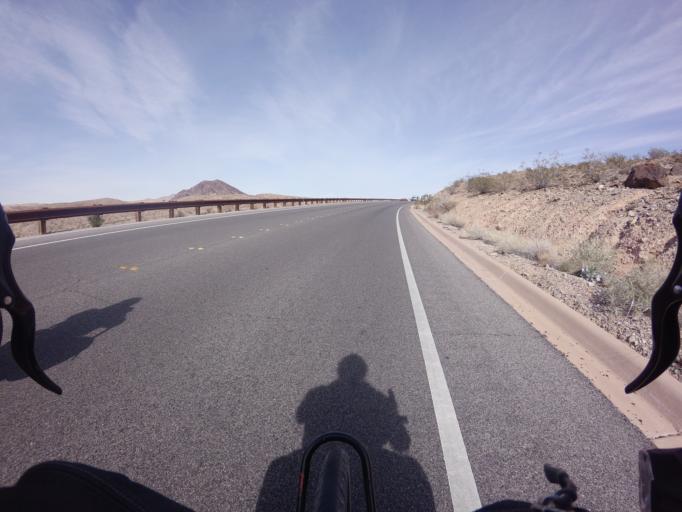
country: US
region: Nevada
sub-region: Clark County
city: Henderson
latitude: 36.1297
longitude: -114.9072
